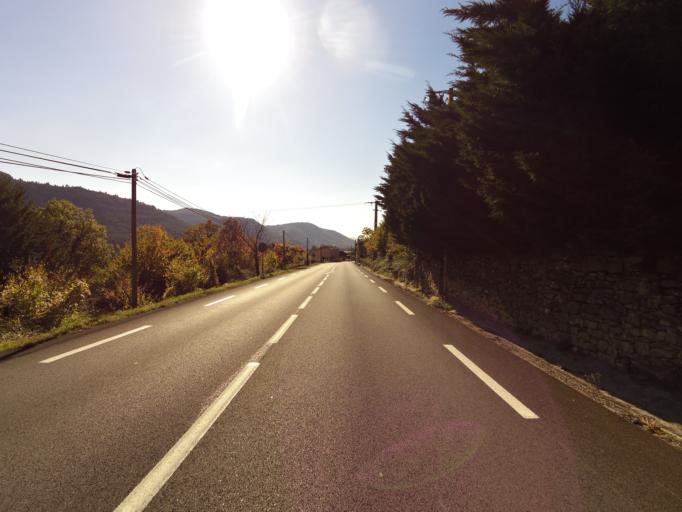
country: FR
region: Rhone-Alpes
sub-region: Departement de l'Ardeche
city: Vesseaux
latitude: 44.6698
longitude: 4.4564
